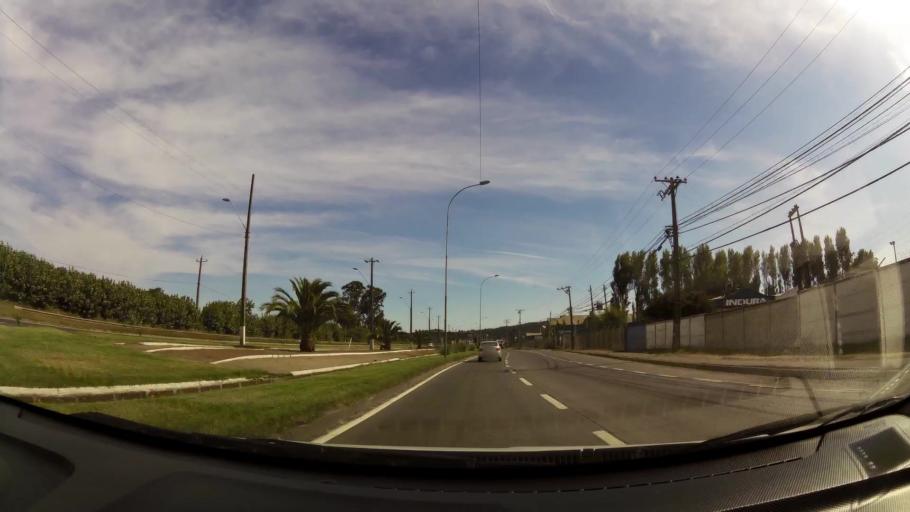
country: CL
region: Biobio
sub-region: Provincia de Concepcion
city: Talcahuano
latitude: -36.7707
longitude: -73.1146
